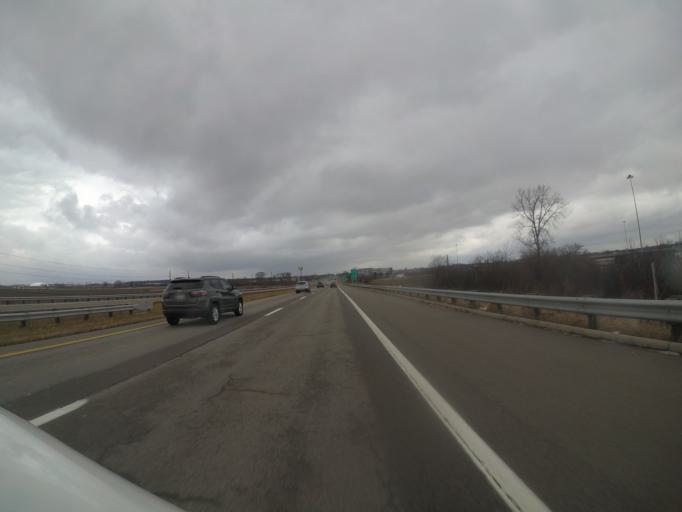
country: US
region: Ohio
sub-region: Wood County
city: Rossford
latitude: 41.5644
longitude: -83.5740
